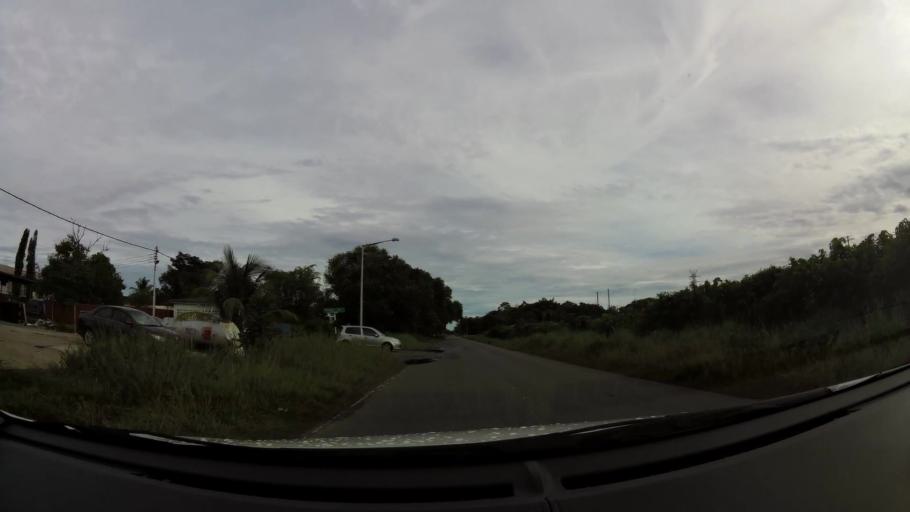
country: BN
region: Belait
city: Seria
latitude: 4.6127
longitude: 114.3392
